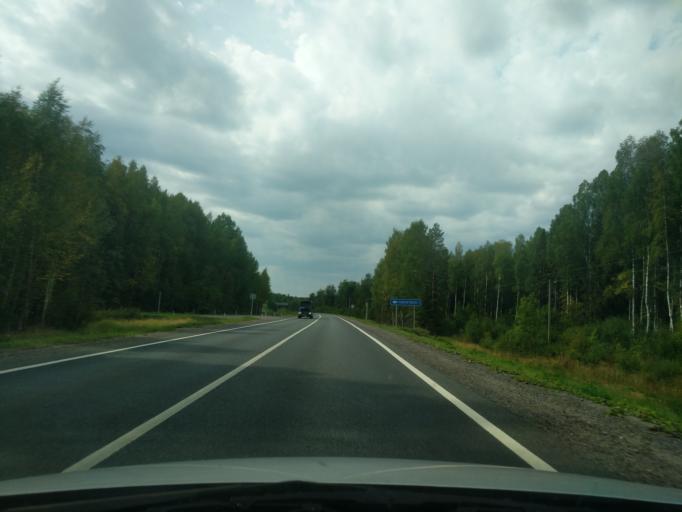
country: RU
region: Kostroma
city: Manturovo
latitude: 58.1659
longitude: 44.4068
